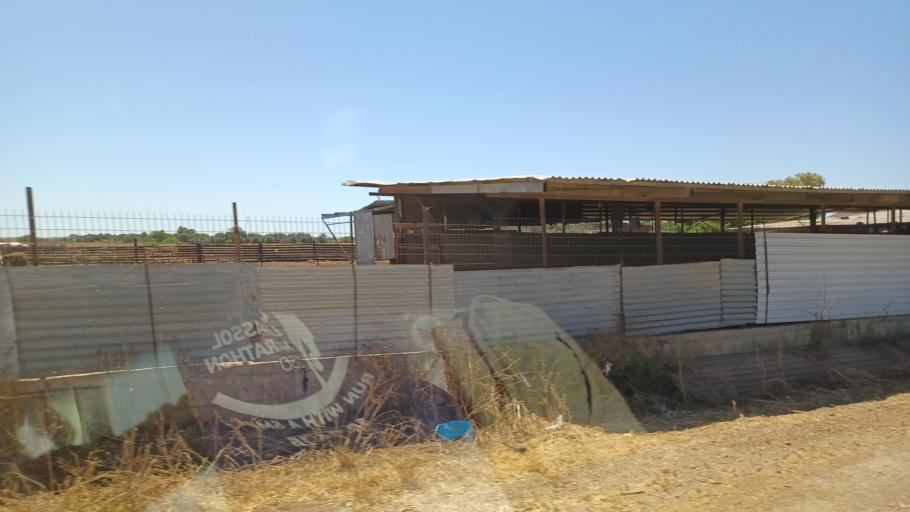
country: CY
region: Ammochostos
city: Avgorou
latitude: 35.0585
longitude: 33.8502
